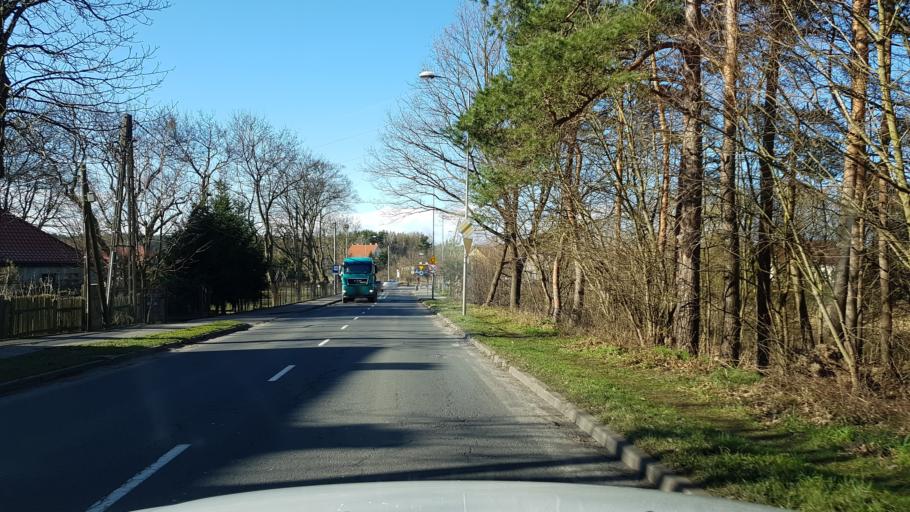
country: PL
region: West Pomeranian Voivodeship
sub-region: Powiat gryfinski
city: Stare Czarnowo
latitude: 53.3551
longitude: 14.7385
